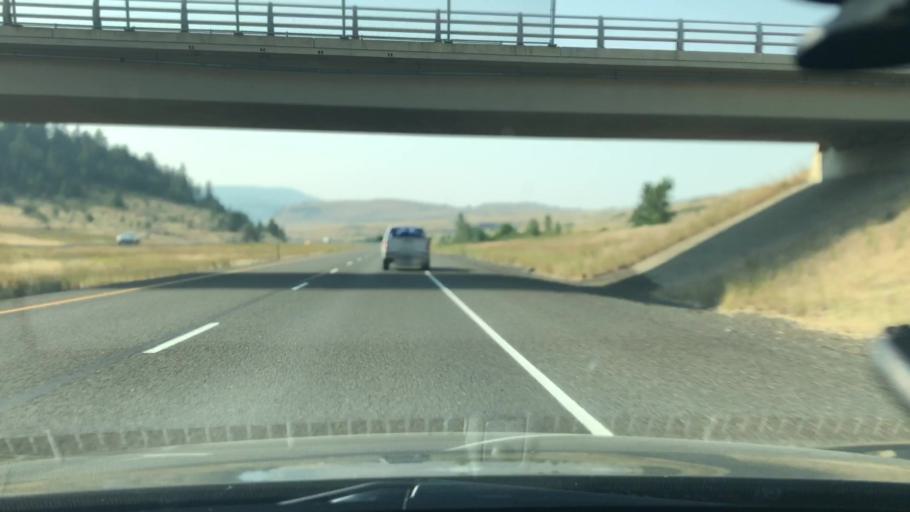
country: US
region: Oregon
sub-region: Union County
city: Union
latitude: 45.1828
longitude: -117.9866
